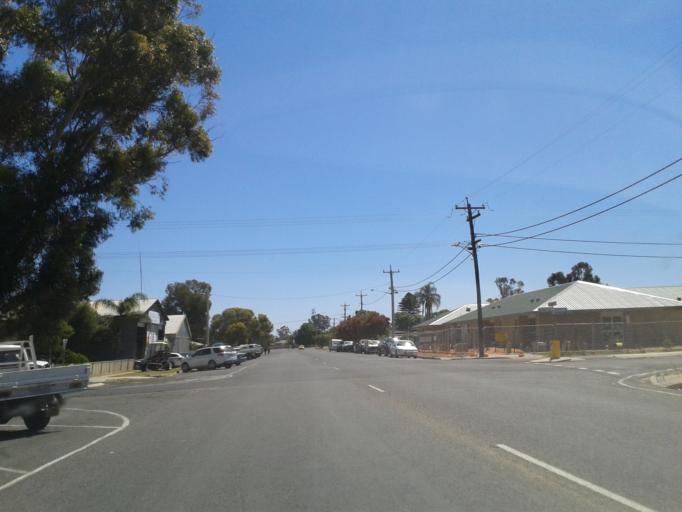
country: AU
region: New South Wales
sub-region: Wentworth
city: Dareton
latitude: -34.1098
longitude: 141.9148
